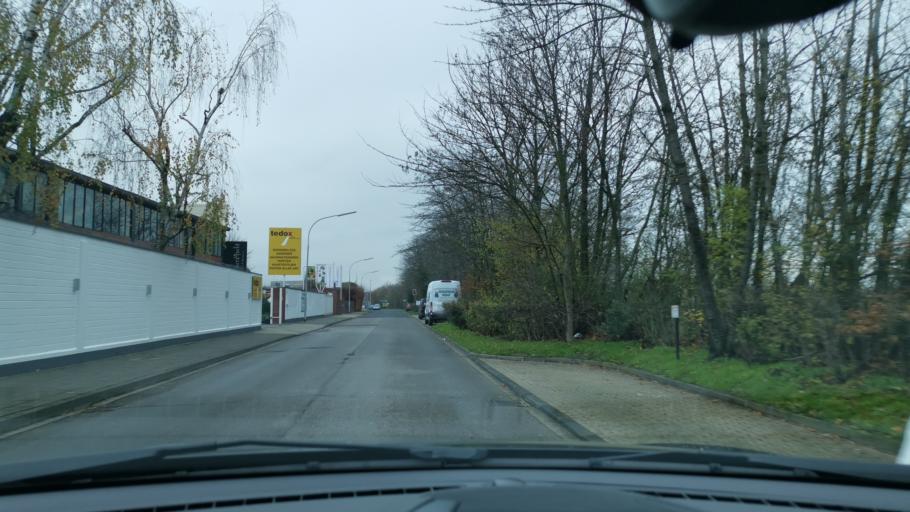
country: DE
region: North Rhine-Westphalia
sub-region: Regierungsbezirk Dusseldorf
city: Neubrueck
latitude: 51.1077
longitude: 6.6317
